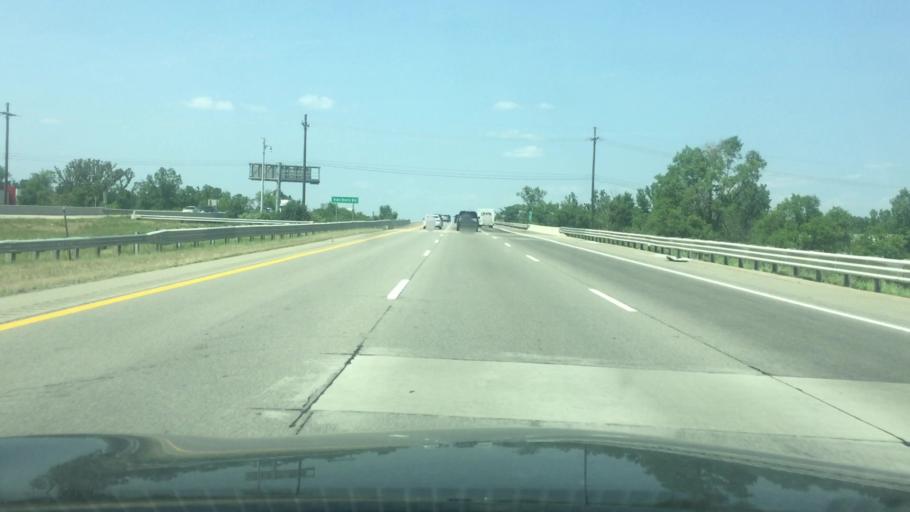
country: US
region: Michigan
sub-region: Wayne County
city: Wayne
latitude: 42.2641
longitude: -83.4405
